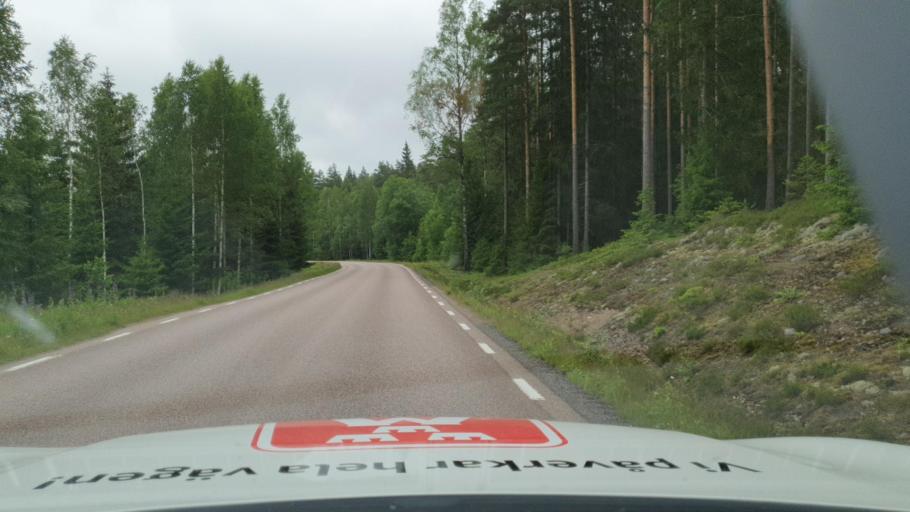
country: SE
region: Vaermland
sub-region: Kristinehamns Kommun
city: Kristinehamn
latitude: 59.4935
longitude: 13.9554
